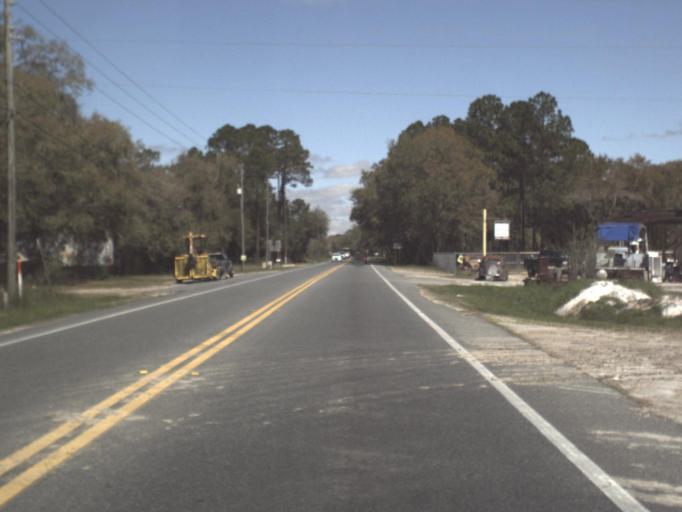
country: US
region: Florida
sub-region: Wakulla County
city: Crawfordville
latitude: 30.0844
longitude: -84.3875
